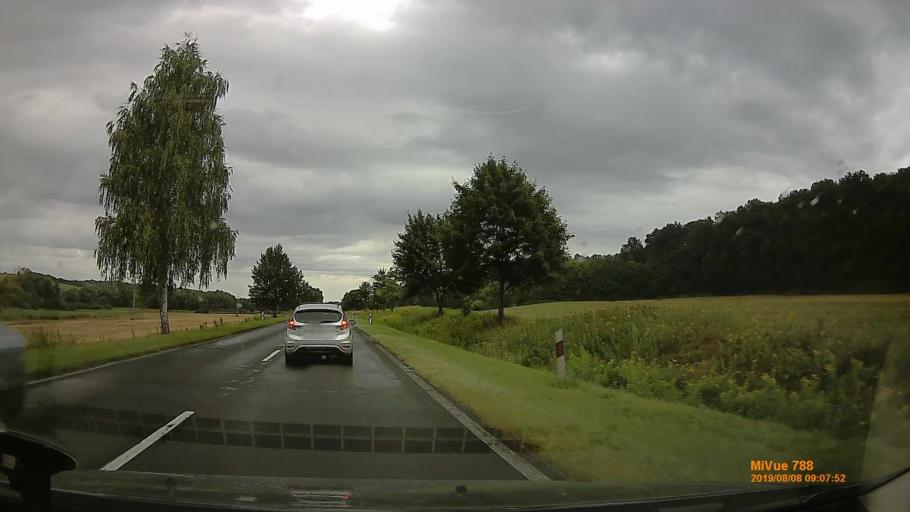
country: HU
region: Zala
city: Zalaegerszeg
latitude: 46.7391
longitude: 16.8559
